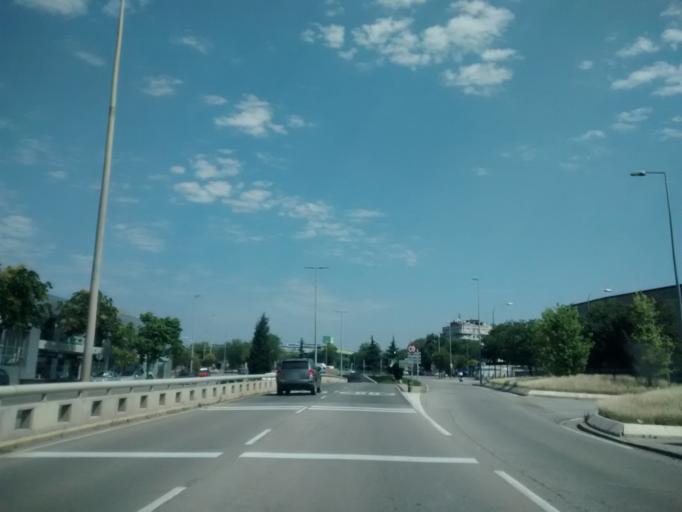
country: ES
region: Catalonia
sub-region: Provincia de Barcelona
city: Sabadell
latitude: 41.5308
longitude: 2.1041
